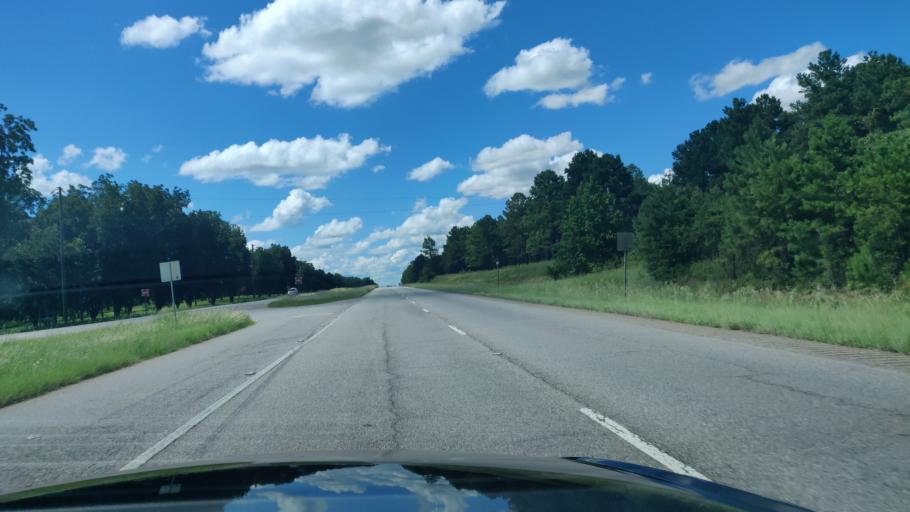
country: US
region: Georgia
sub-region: Stewart County
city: Richland
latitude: 32.0301
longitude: -84.6744
